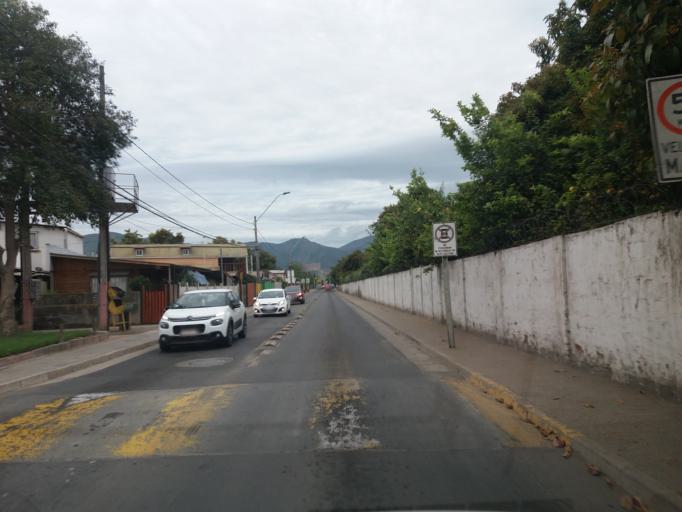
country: CL
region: Valparaiso
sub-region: Provincia de Quillota
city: Quillota
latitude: -32.8424
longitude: -71.2272
